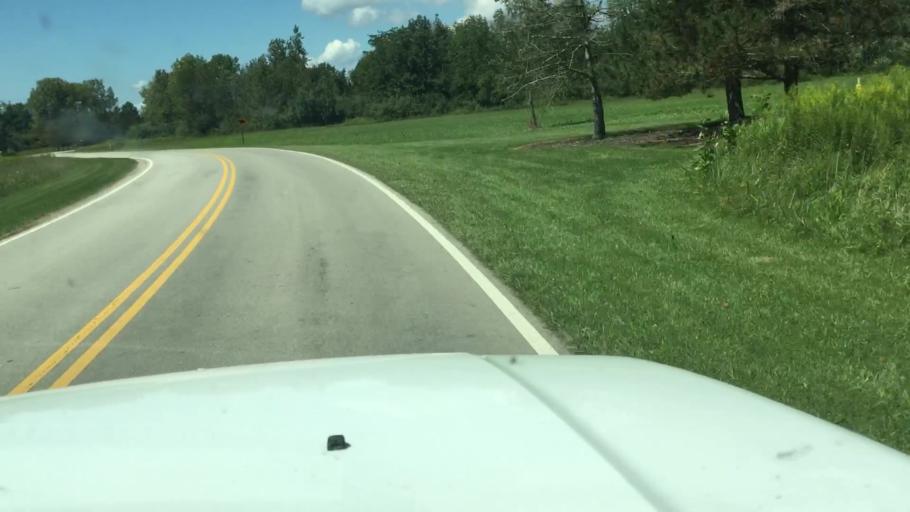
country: US
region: Ohio
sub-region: Madison County
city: Mount Sterling
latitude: 39.6424
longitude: -83.2443
